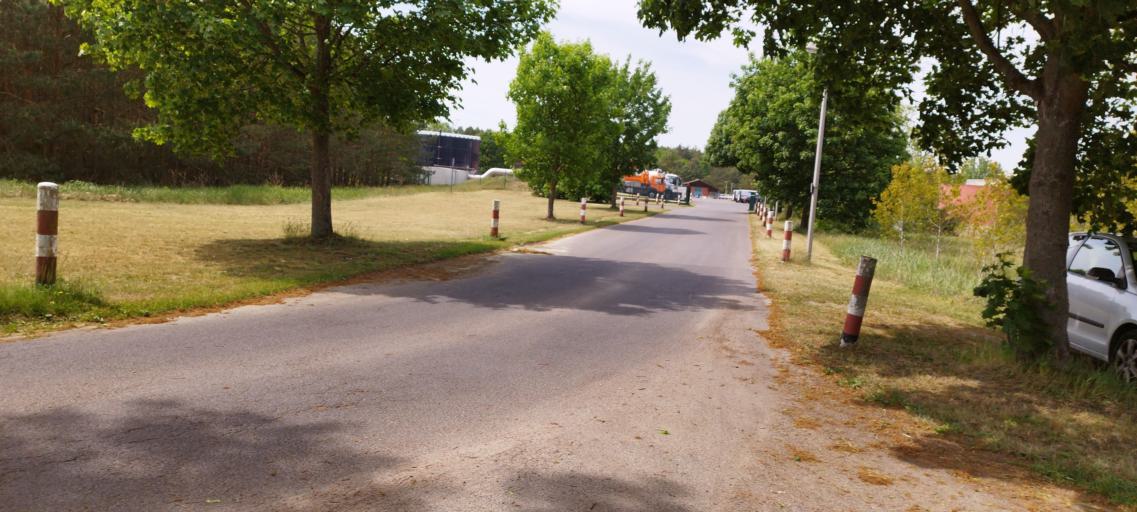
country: DE
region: Brandenburg
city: Rauen
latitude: 52.3772
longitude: 14.0114
